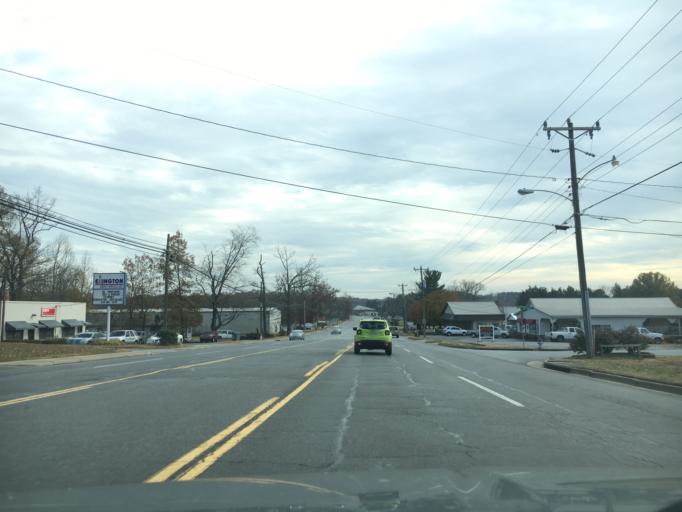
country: US
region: Virginia
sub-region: Prince Edward County
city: Farmville
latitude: 37.3094
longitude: -78.4184
